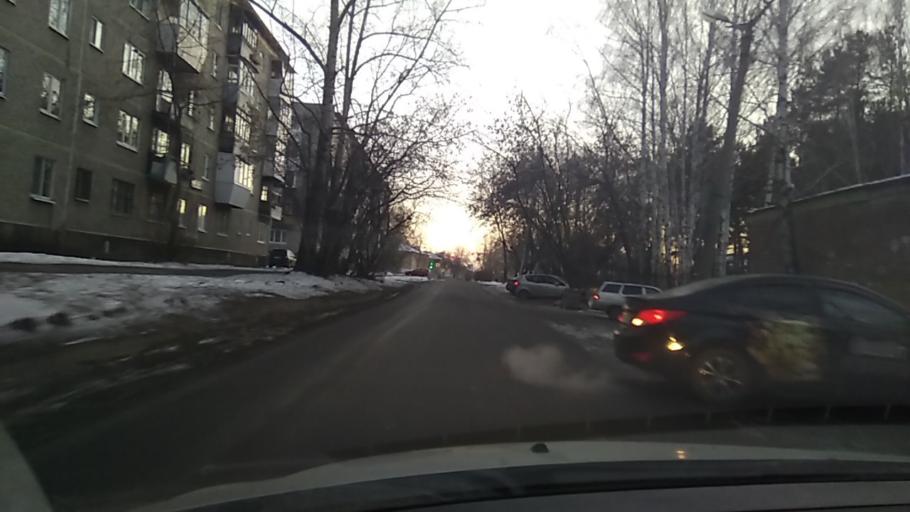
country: RU
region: Sverdlovsk
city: Istok
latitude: 56.7639
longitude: 60.7109
